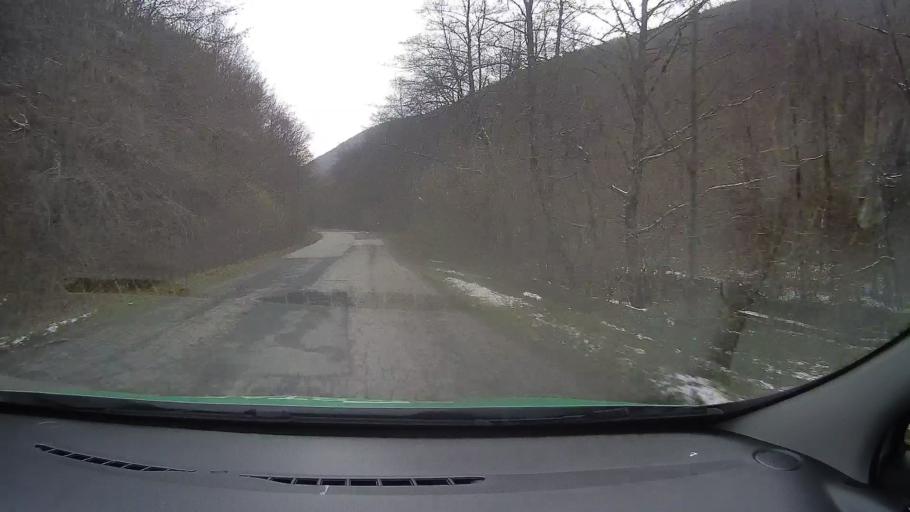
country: RO
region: Hunedoara
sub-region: Comuna Balsa
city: Balsa
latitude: 45.9978
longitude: 23.1509
